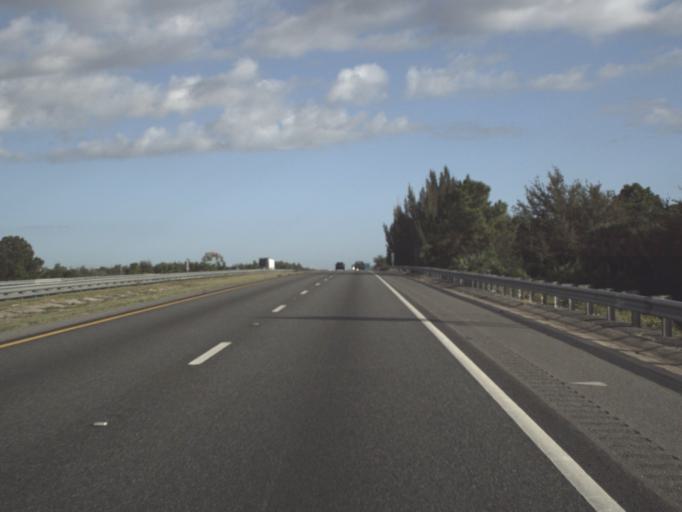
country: US
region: Florida
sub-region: Orange County
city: Southchase
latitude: 28.4041
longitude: -81.3913
